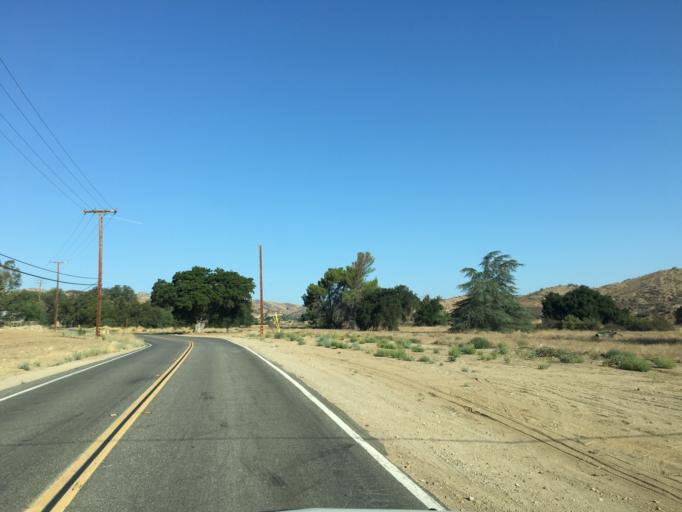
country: US
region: California
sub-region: Los Angeles County
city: Val Verde
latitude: 34.4592
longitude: -118.6481
